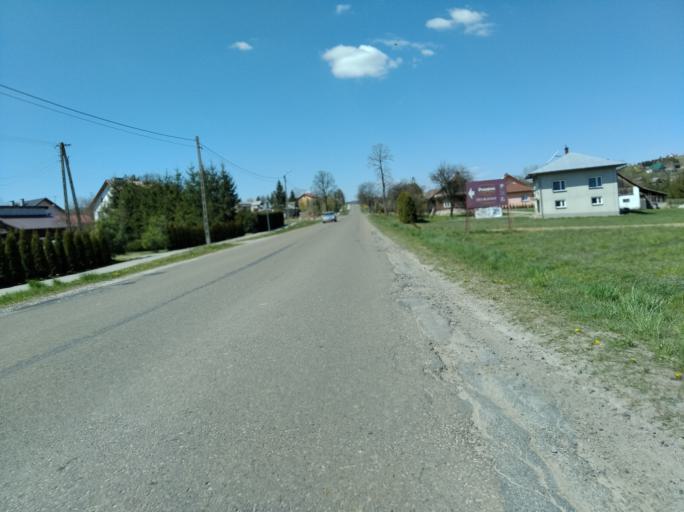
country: PL
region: Subcarpathian Voivodeship
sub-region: Powiat brzozowski
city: Dydnia
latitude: 49.6891
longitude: 22.1642
